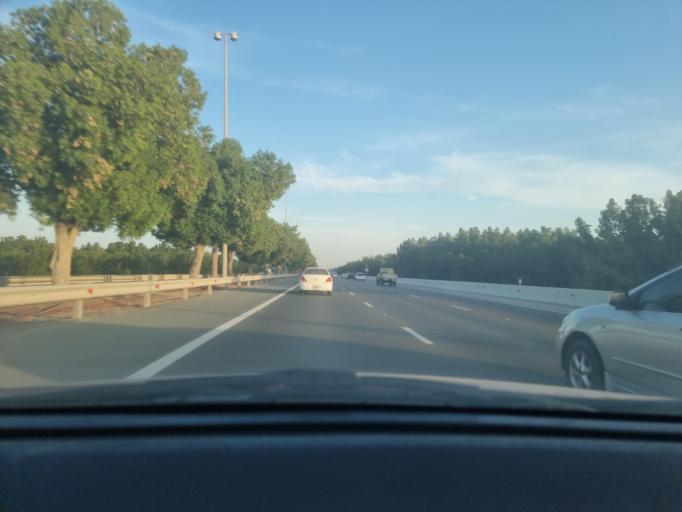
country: AE
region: Abu Dhabi
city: Abu Dhabi
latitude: 24.2680
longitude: 54.6684
